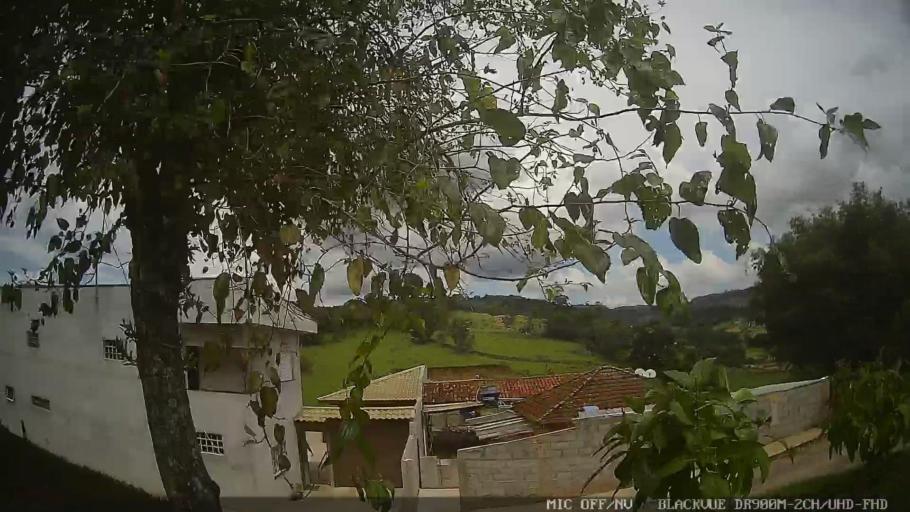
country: BR
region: Minas Gerais
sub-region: Extrema
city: Extrema
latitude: -22.7449
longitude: -46.3722
